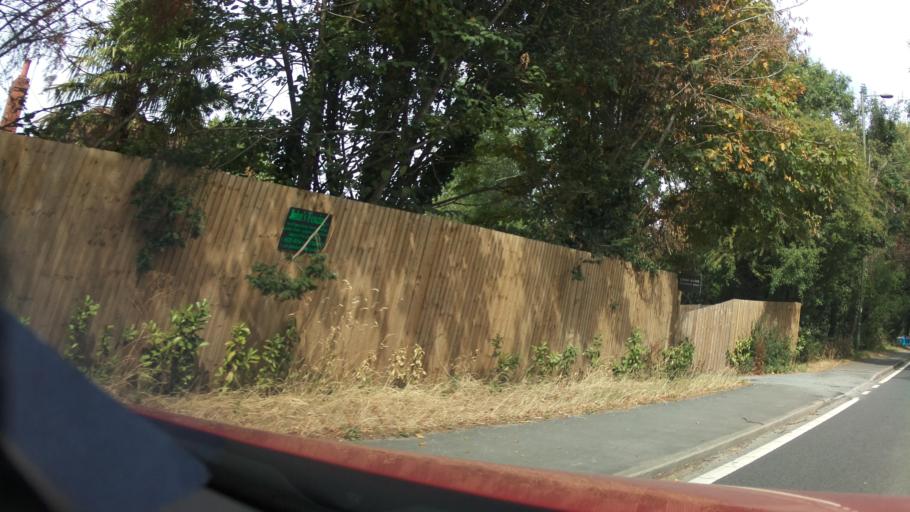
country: GB
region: England
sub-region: Surrey
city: Salfords
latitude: 51.1808
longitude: -0.1953
